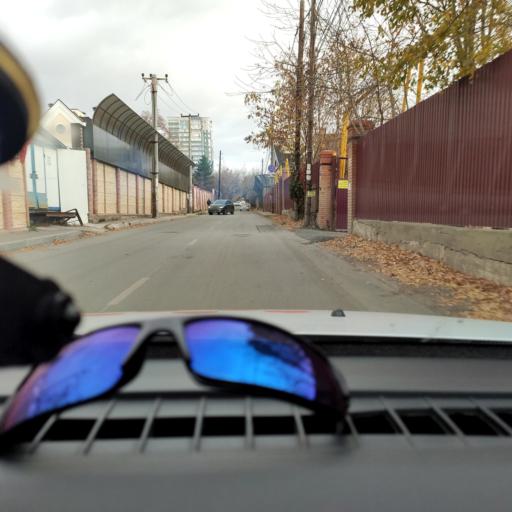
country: RU
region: Samara
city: Samara
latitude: 53.2361
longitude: 50.1752
